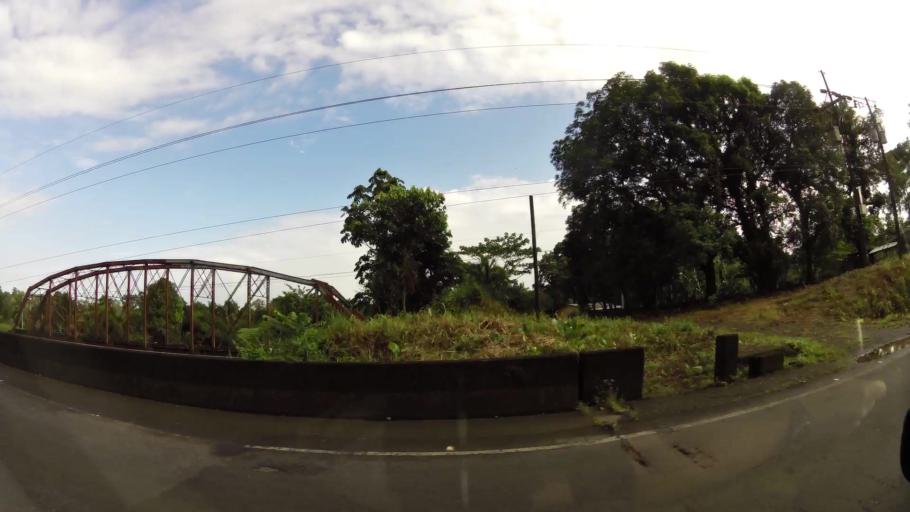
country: CR
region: Limon
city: Pocora
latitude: 10.1950
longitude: -83.6446
